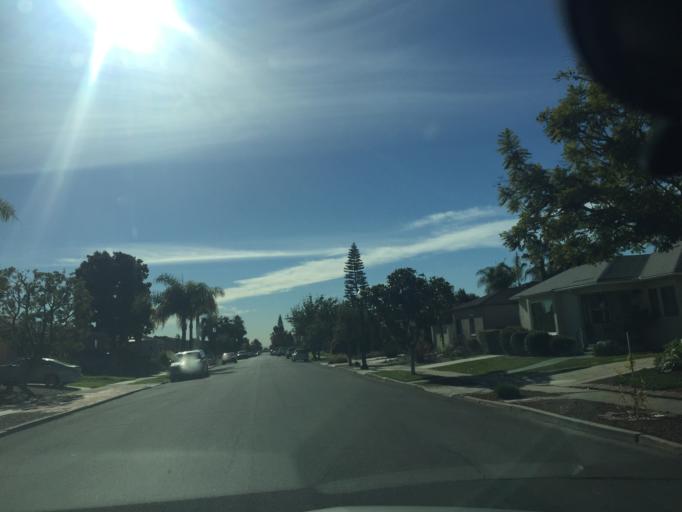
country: US
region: California
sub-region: San Diego County
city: Lemon Grove
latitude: 32.7620
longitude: -117.0889
